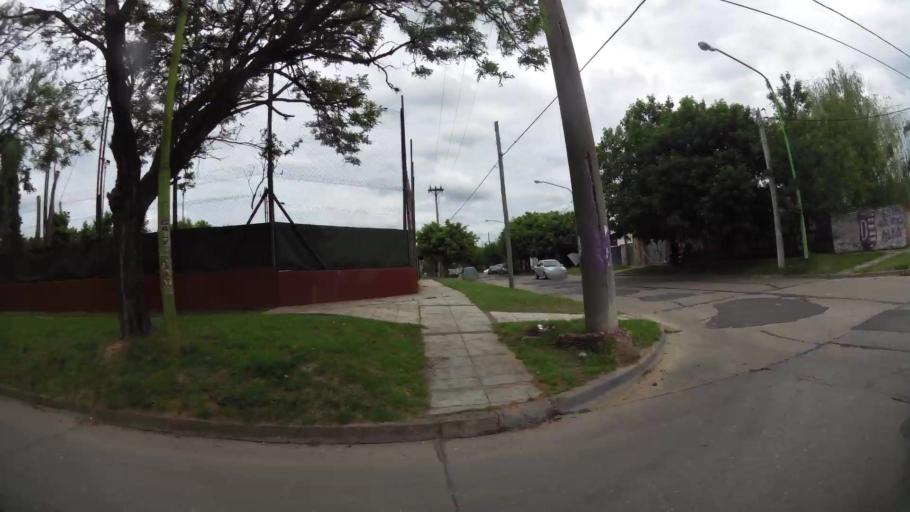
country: AR
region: Buenos Aires
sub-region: Partido de Campana
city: Campana
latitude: -34.1697
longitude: -58.9632
